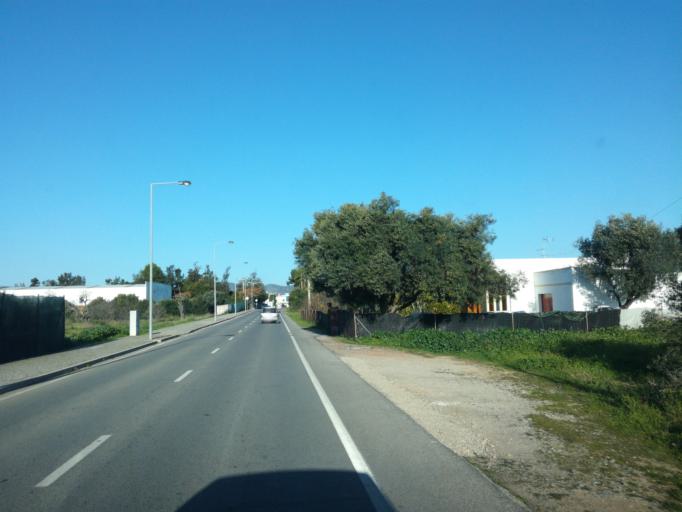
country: PT
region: Faro
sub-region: Olhao
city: Laranjeiro
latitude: 37.0556
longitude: -7.7596
